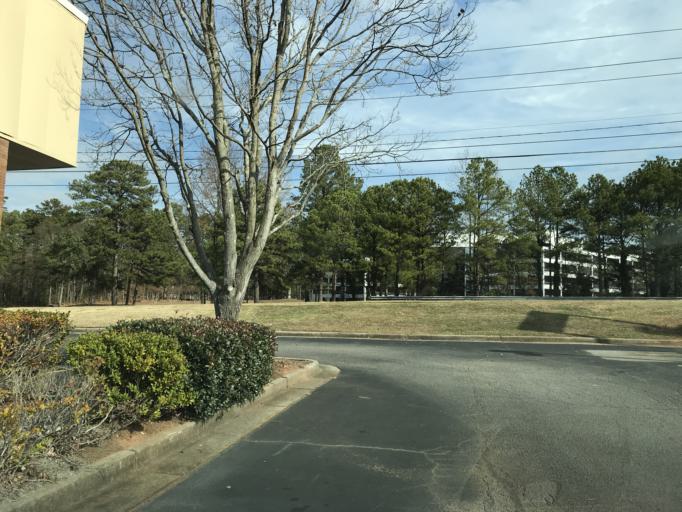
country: US
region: Georgia
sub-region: DeKalb County
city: Tucker
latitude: 33.8420
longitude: -84.2435
